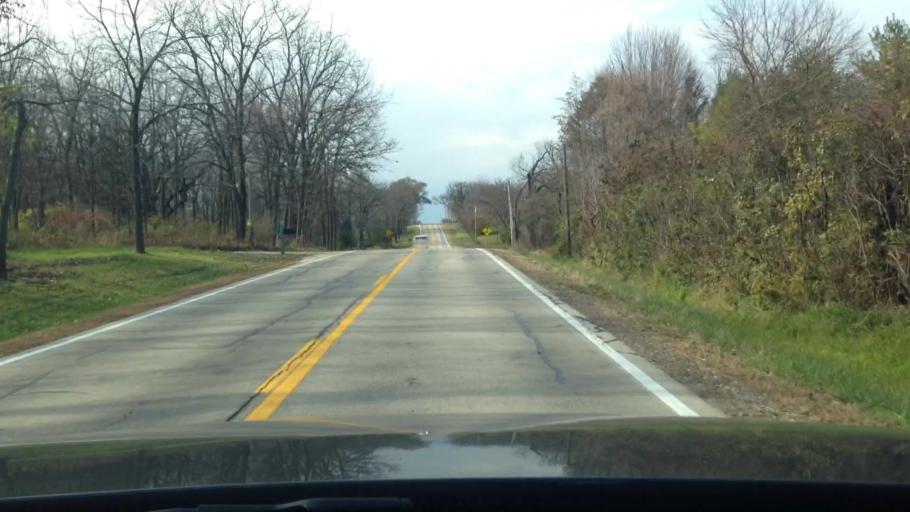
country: US
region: Illinois
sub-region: McHenry County
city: Woodstock
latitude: 42.2984
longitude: -88.4648
